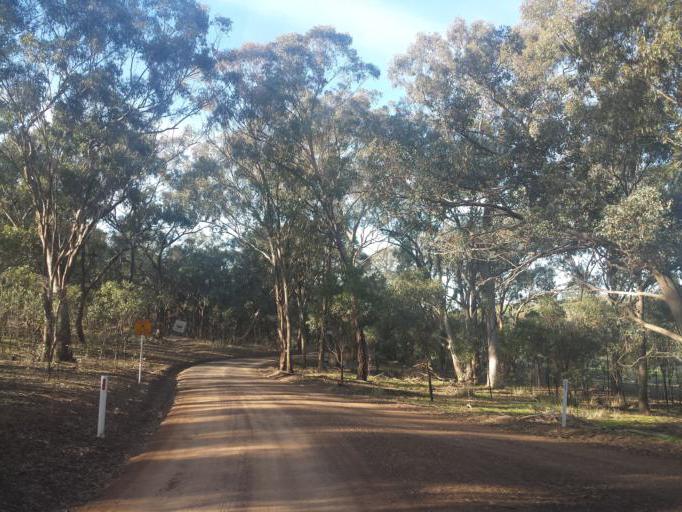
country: AU
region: Victoria
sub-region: Murrindindi
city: Kinglake West
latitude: -37.0265
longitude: 145.2097
